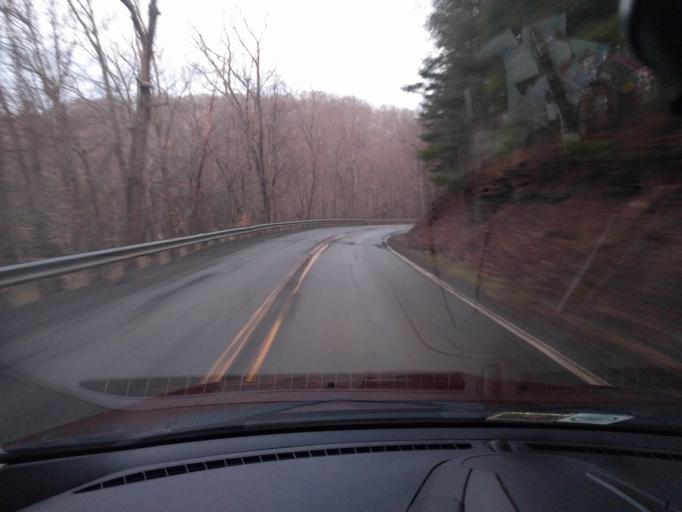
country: US
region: West Virginia
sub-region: Greenbrier County
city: Rainelle
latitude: 37.9955
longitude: -80.8672
